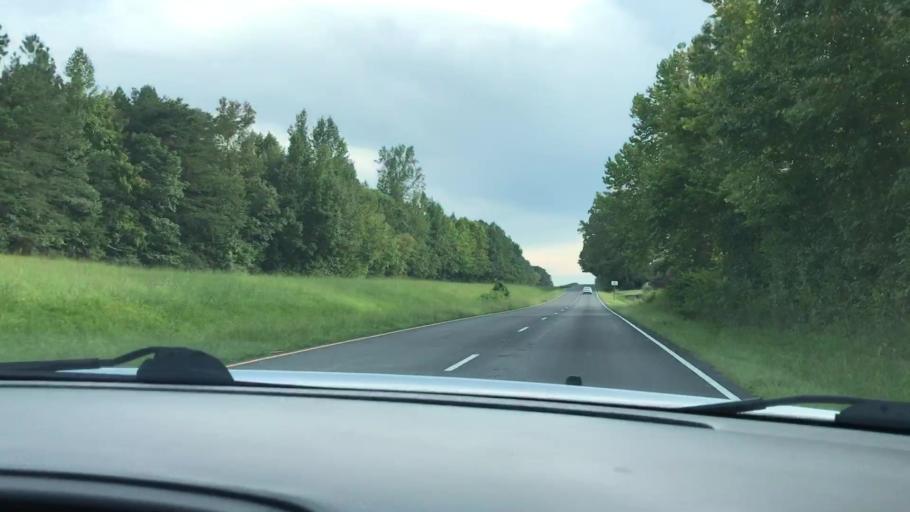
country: US
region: North Carolina
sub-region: Davidson County
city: Denton
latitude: 35.6171
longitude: -80.0132
